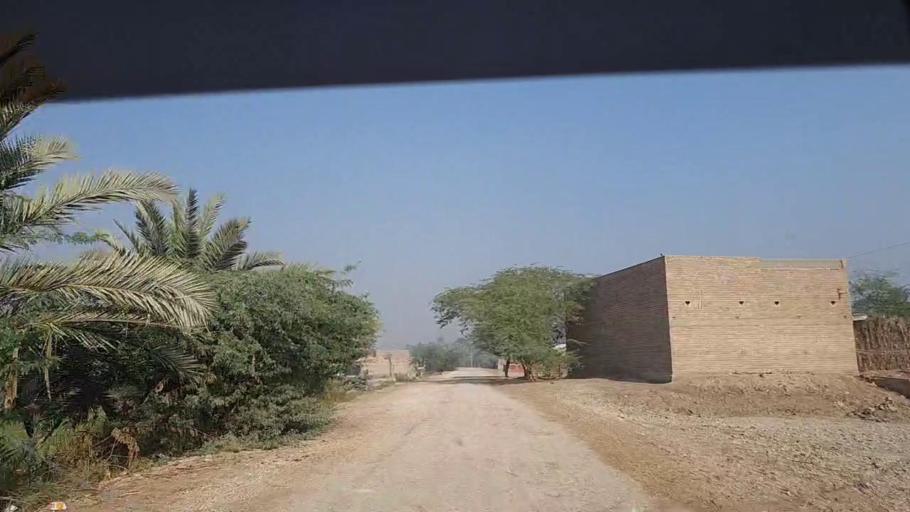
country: PK
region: Sindh
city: Khairpur
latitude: 27.4959
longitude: 68.7370
